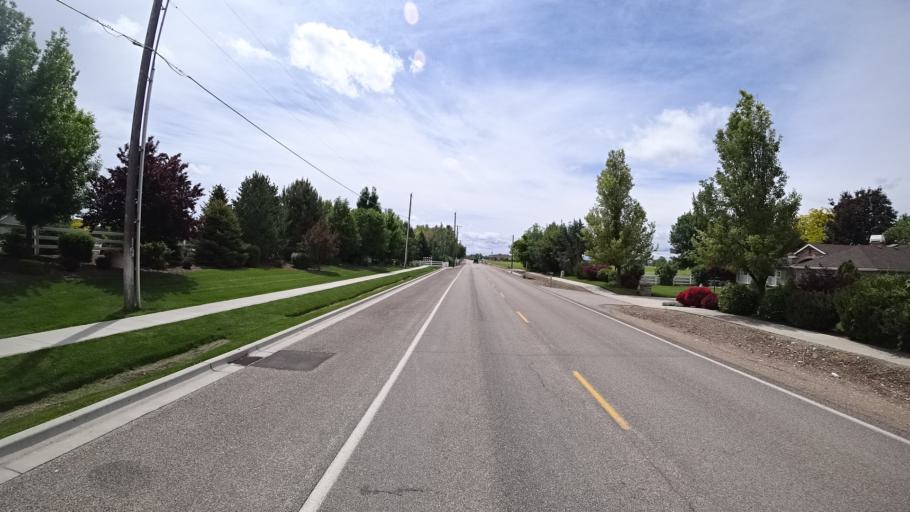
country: US
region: Idaho
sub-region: Ada County
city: Eagle
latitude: 43.7106
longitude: -116.4035
